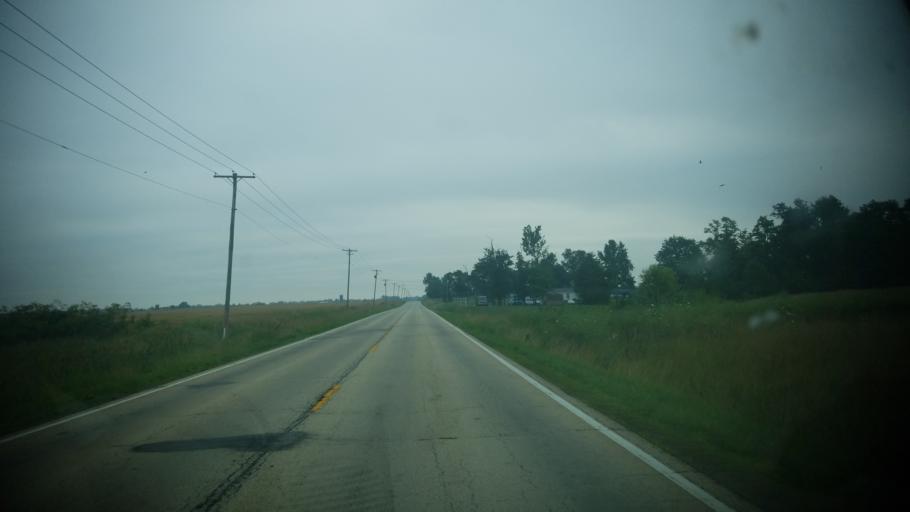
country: US
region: Illinois
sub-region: Clay County
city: Flora
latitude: 38.6539
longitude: -88.4384
